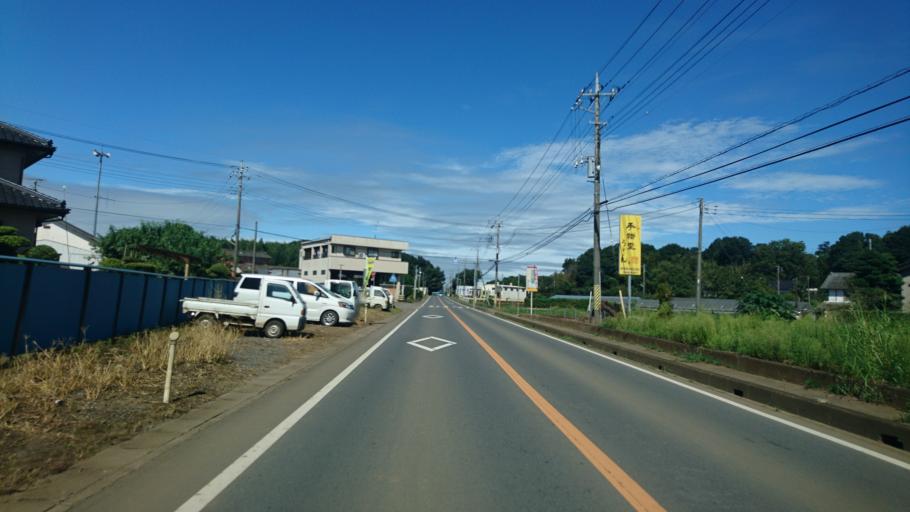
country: JP
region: Ibaraki
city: Ishige
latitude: 36.1445
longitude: 139.9047
